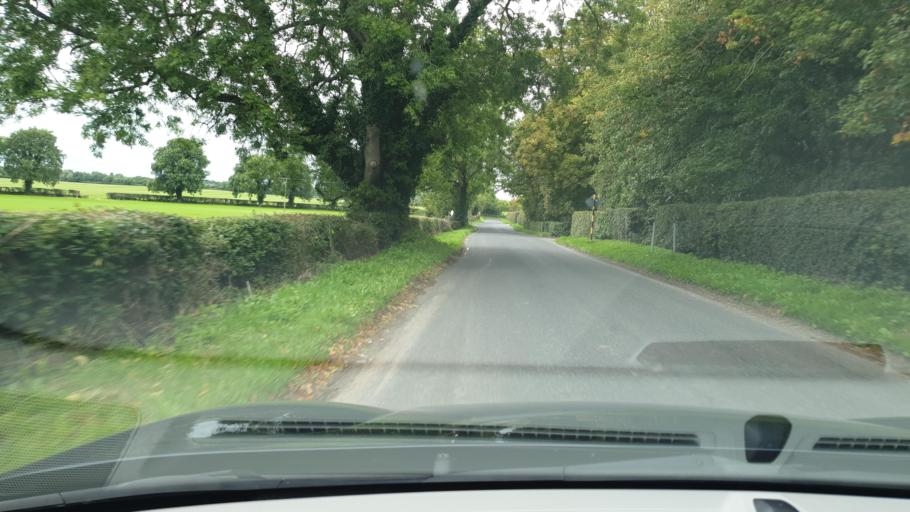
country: IE
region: Leinster
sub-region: Kildare
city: Maynooth
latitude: 53.3664
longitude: -6.6215
